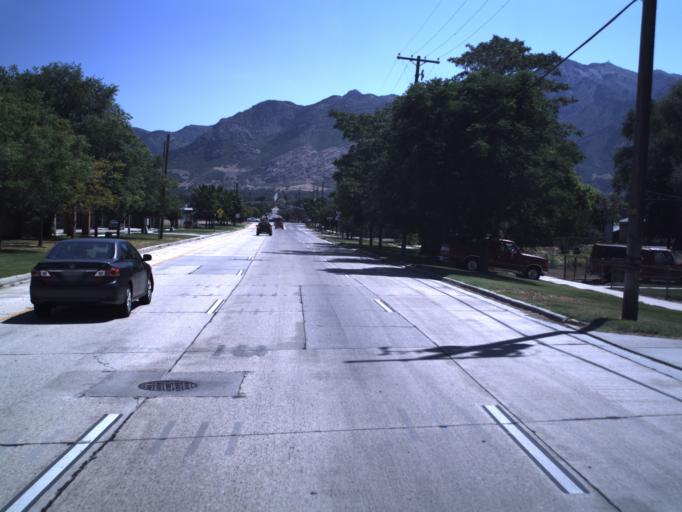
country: US
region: Utah
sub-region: Weber County
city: Ogden
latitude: 41.2292
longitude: -111.9824
